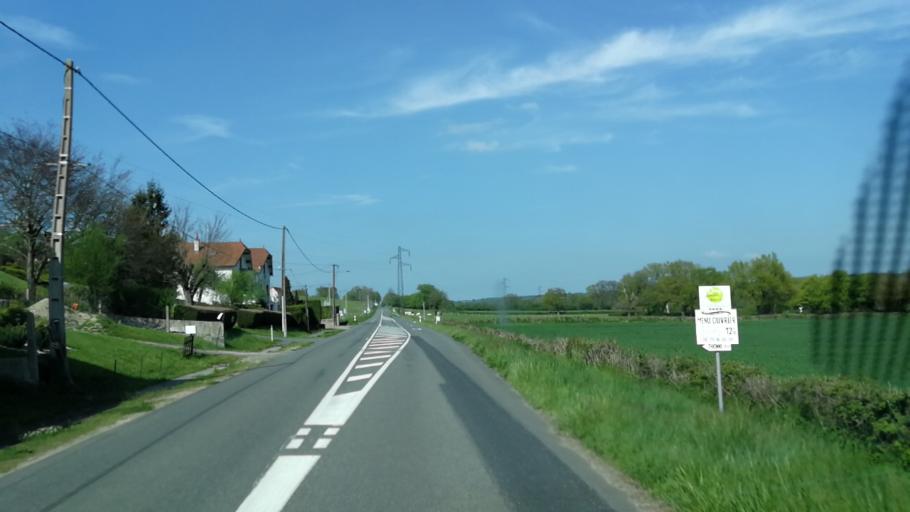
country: FR
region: Auvergne
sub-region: Departement de l'Allier
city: Lapalisse
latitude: 46.3854
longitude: 3.5855
